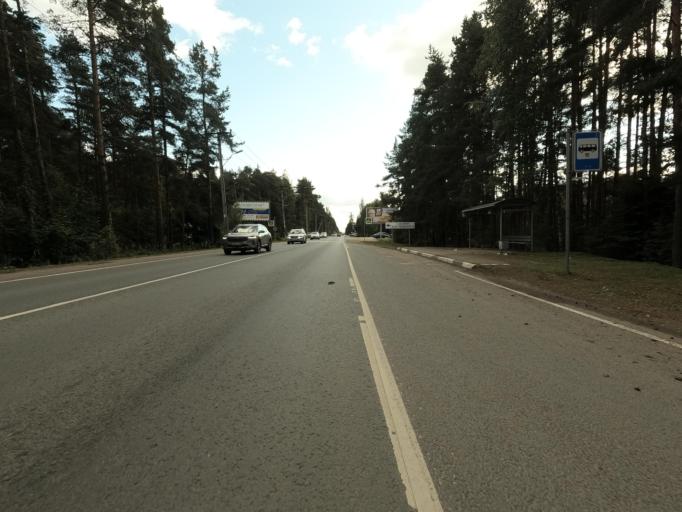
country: RU
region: Leningrad
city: Vsevolozhsk
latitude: 60.0011
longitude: 30.6621
